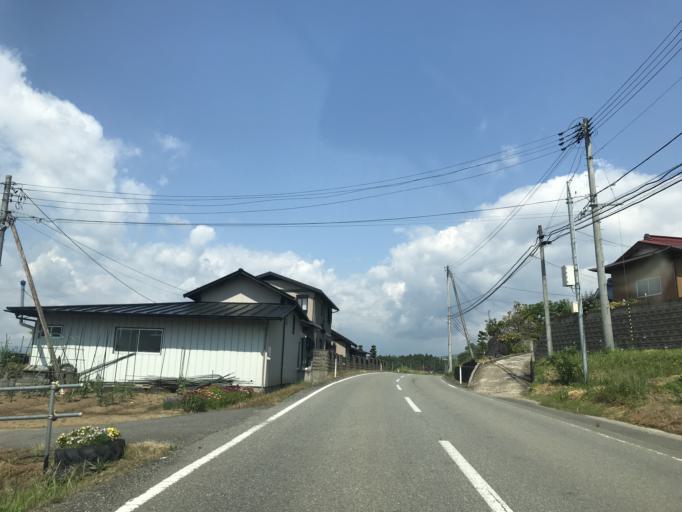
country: JP
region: Iwate
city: Ichinoseki
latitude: 38.8008
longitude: 141.0148
